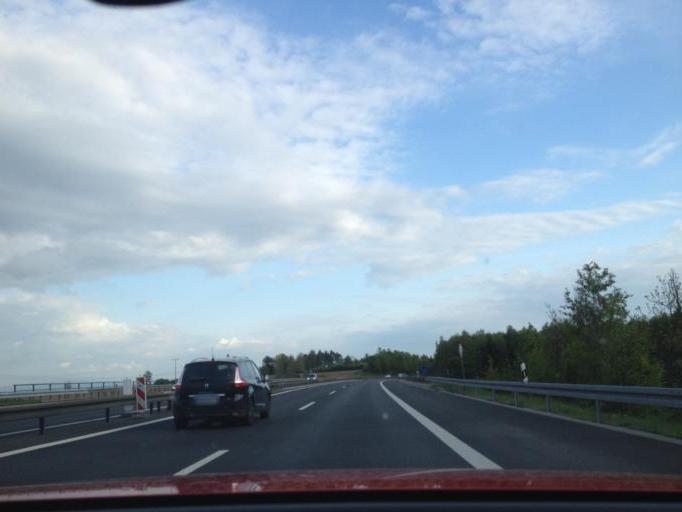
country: DE
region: Bavaria
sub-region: Upper Palatinate
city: Mitterteich
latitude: 49.9315
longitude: 12.2259
